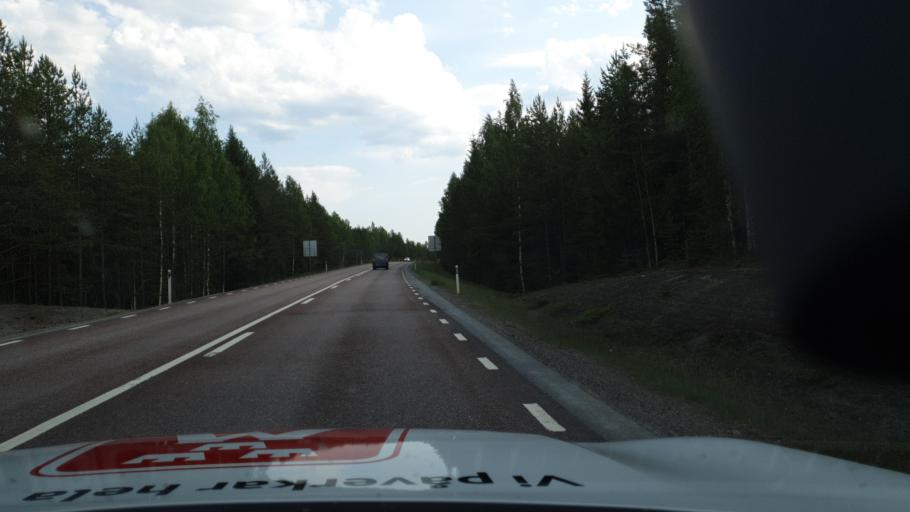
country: SE
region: Vaesterbotten
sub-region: Skelleftea Kommun
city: Burea
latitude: 64.6297
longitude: 21.1770
